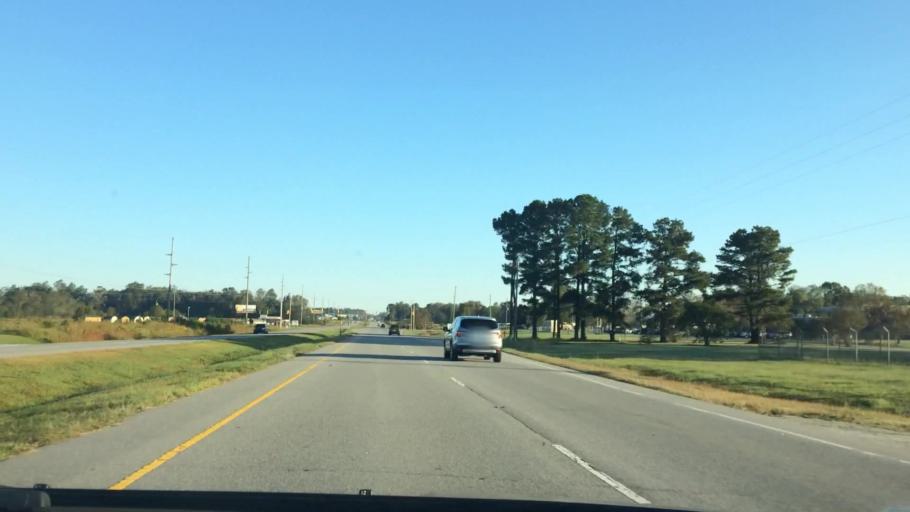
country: US
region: North Carolina
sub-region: Pitt County
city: Ayden
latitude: 35.4285
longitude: -77.4335
